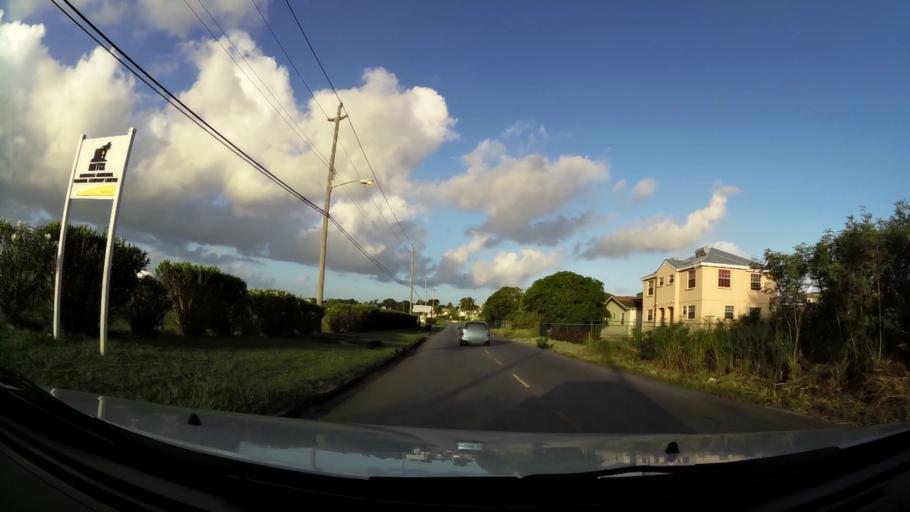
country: BB
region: Christ Church
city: Oistins
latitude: 13.0807
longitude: -59.4991
